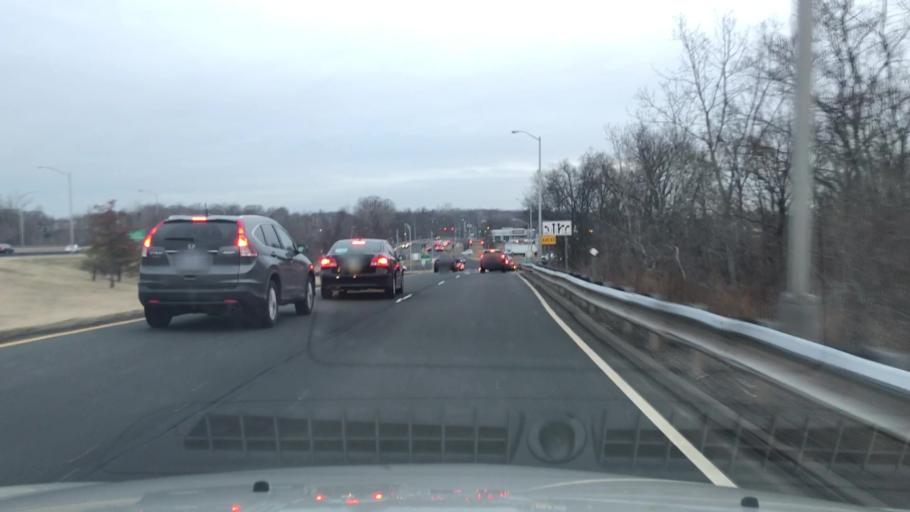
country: US
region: Connecticut
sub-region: Hartford County
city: Newington
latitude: 41.6917
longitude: -72.7568
